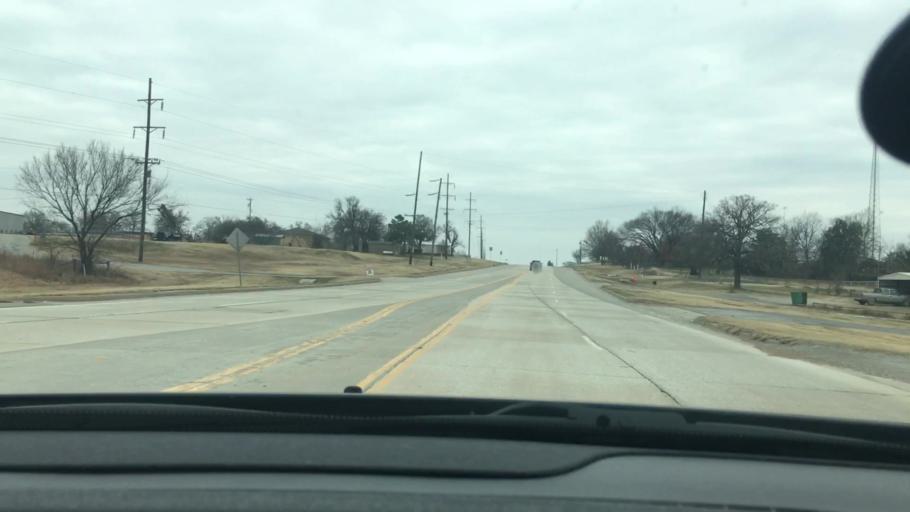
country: US
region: Oklahoma
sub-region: Carter County
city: Healdton
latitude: 34.4469
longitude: -97.5097
